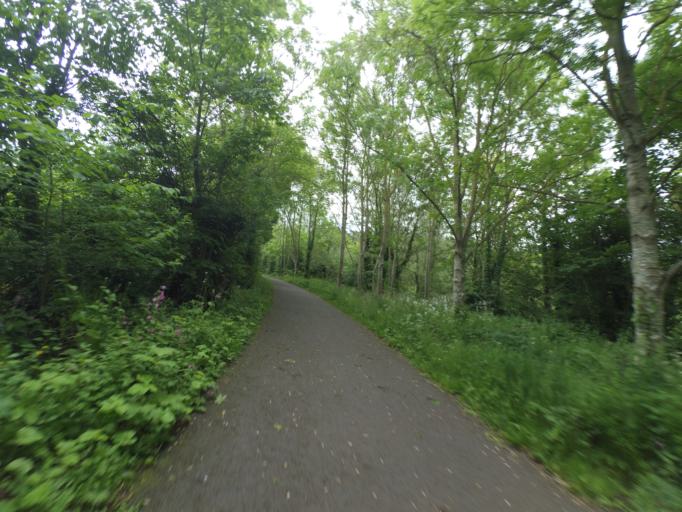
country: GB
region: Scotland
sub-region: East Lothian
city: Musselburgh
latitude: 55.9275
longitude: -3.0496
